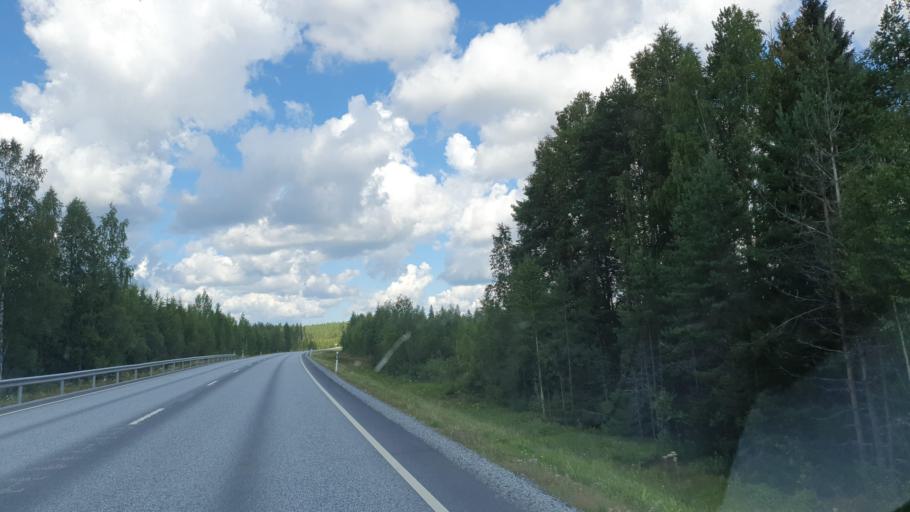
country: FI
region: Northern Savo
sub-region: Ylae-Savo
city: Sonkajaervi
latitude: 63.9104
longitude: 27.3858
